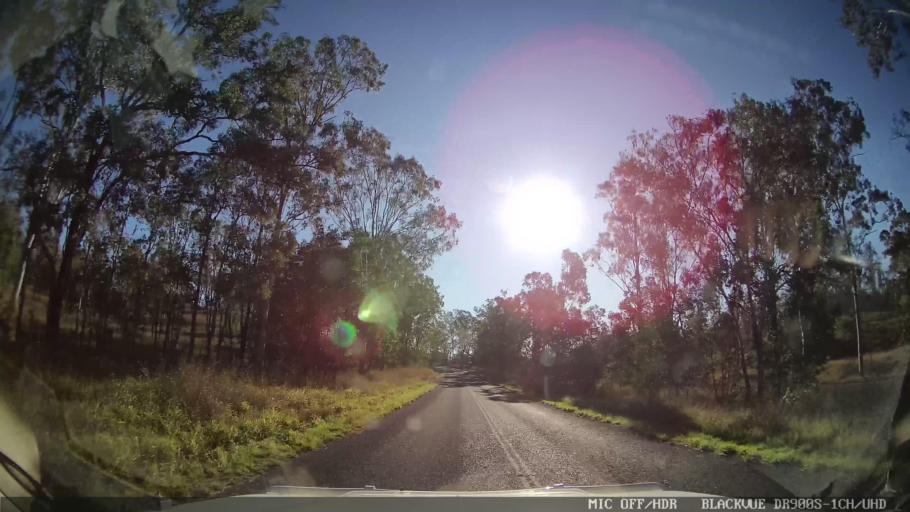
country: AU
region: Queensland
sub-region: Bundaberg
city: Sharon
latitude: -24.8057
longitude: 151.6588
